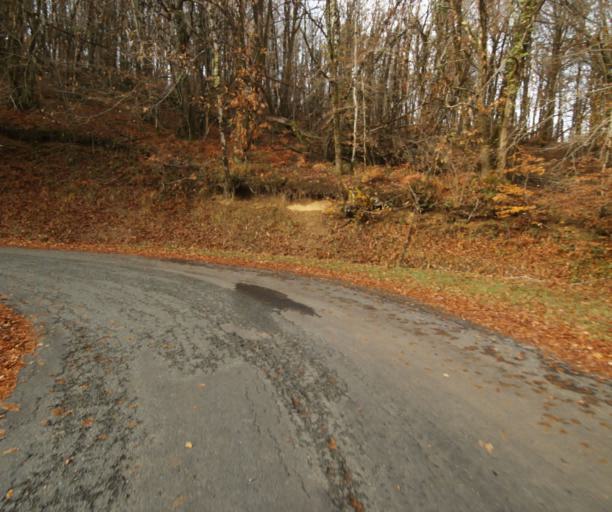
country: FR
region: Limousin
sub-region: Departement de la Correze
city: Chameyrat
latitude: 45.2211
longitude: 1.7183
